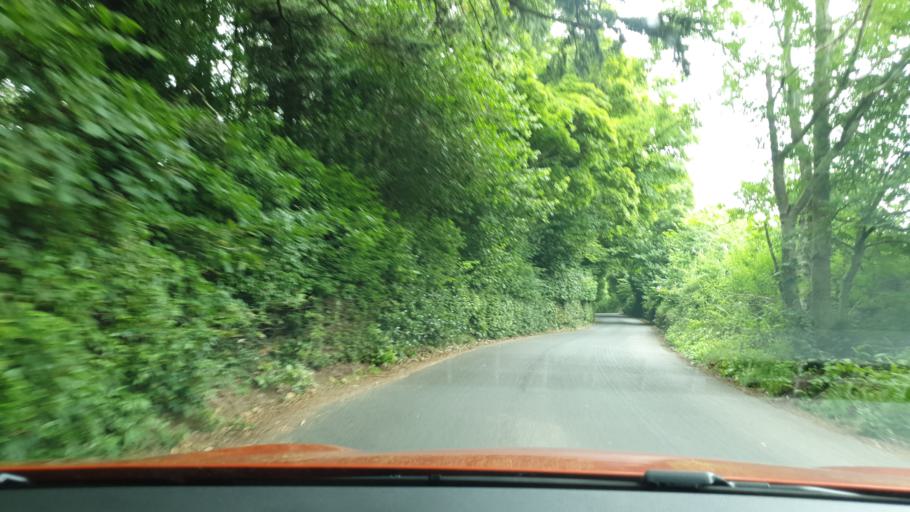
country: GB
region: England
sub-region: Cumbria
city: Penrith
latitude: 54.5890
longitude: -2.8431
